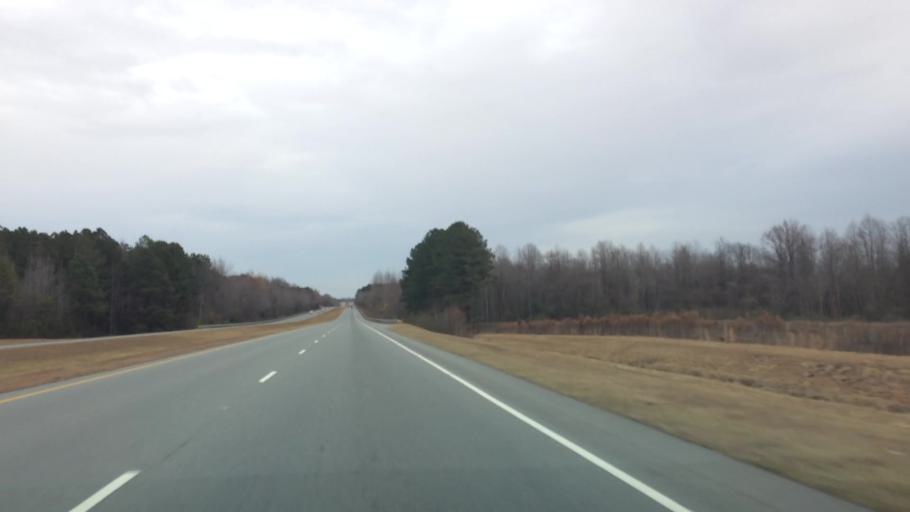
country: US
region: North Carolina
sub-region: Wayne County
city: Mount Olive
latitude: 35.1347
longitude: -78.1406
